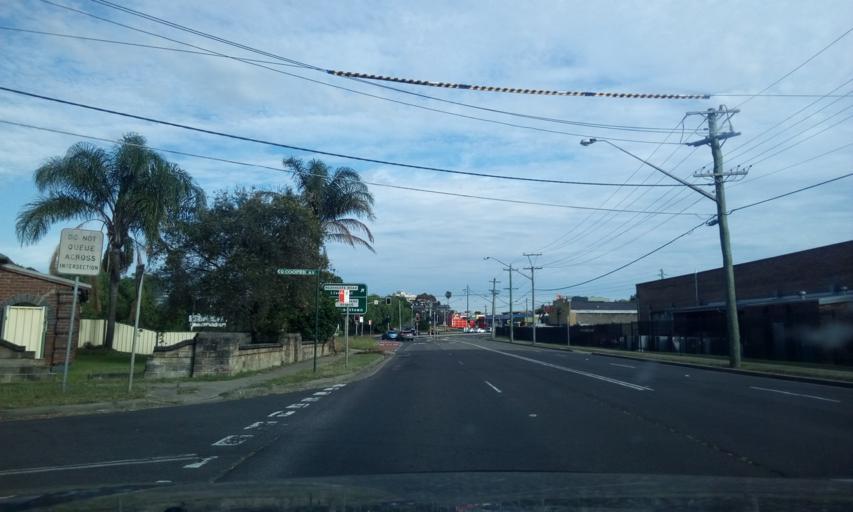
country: AU
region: New South Wales
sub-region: Fairfield
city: Liverpool
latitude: -33.9302
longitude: 150.9322
